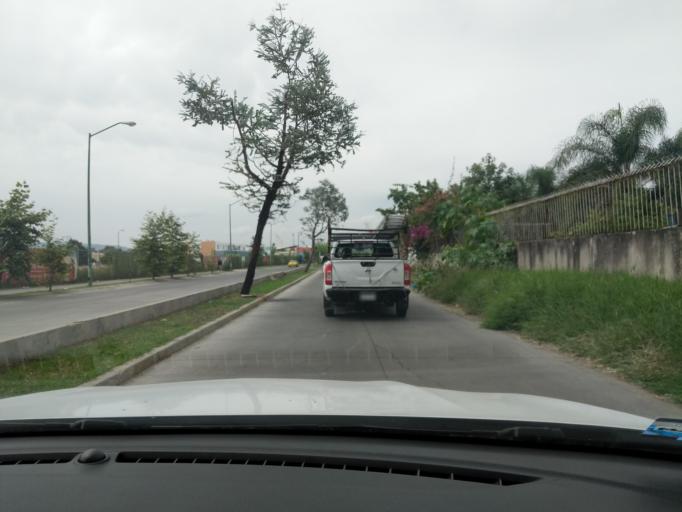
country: MX
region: Jalisco
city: Tesistan
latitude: 20.7902
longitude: -103.4868
